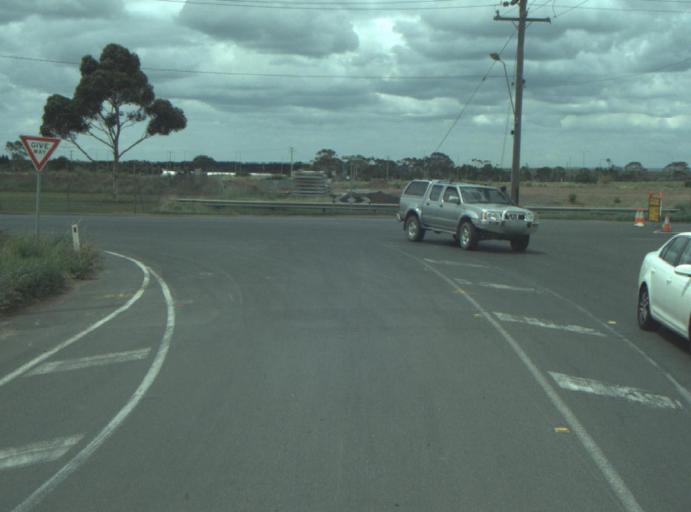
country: AU
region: Victoria
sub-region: Greater Geelong
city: Lara
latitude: -38.0519
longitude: 144.3907
